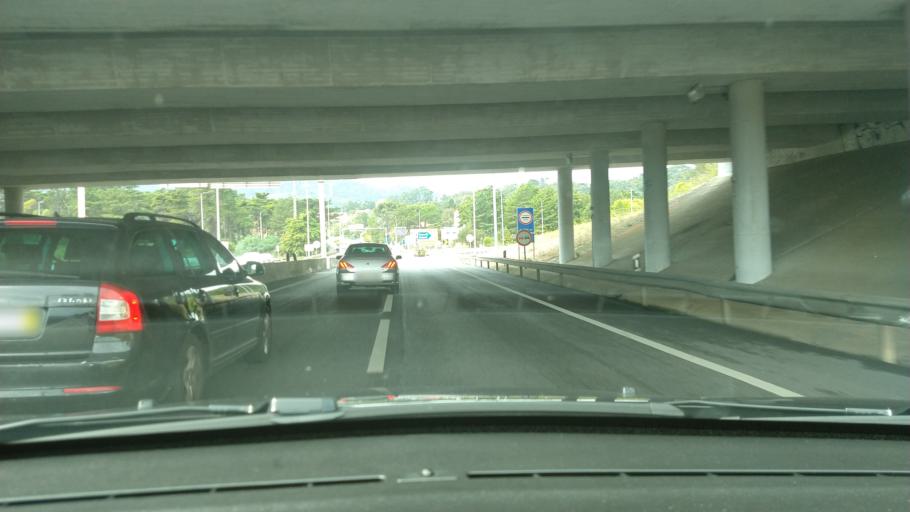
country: PT
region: Lisbon
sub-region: Sintra
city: Sintra
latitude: 38.7828
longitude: -9.3623
